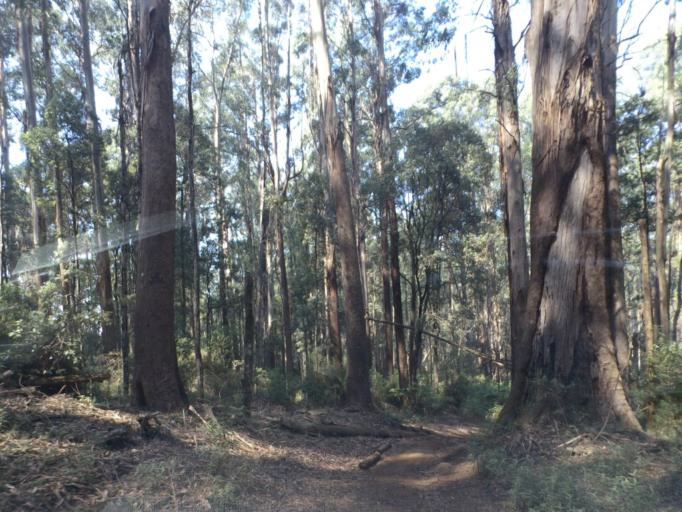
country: AU
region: Victoria
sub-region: Yarra Ranges
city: Healesville
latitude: -37.5637
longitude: 145.6145
